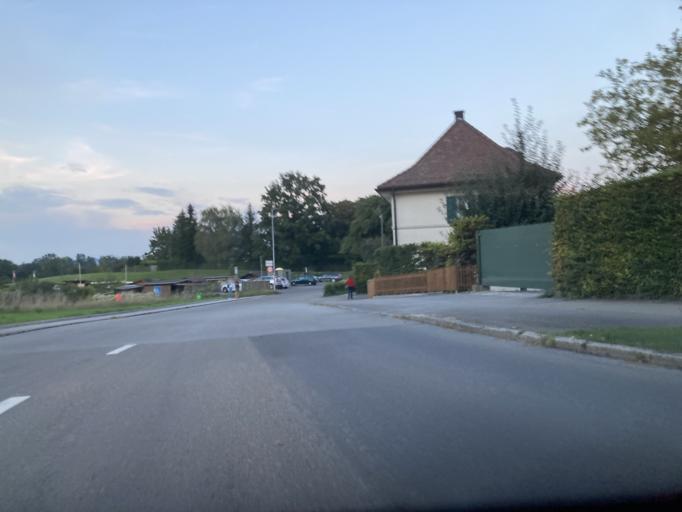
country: CH
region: Zurich
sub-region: Bezirk Horgen
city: Ruschlikon
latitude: 47.3105
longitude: 8.5449
